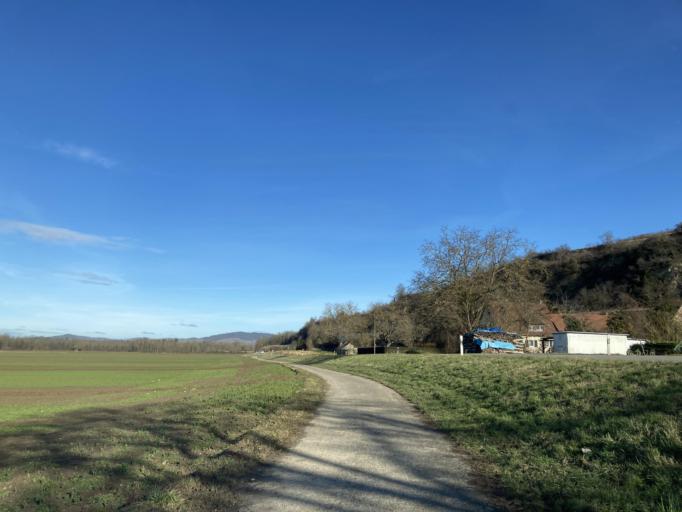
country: DE
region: Baden-Wuerttemberg
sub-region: Freiburg Region
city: Merdingen
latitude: 47.9918
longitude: 7.6712
